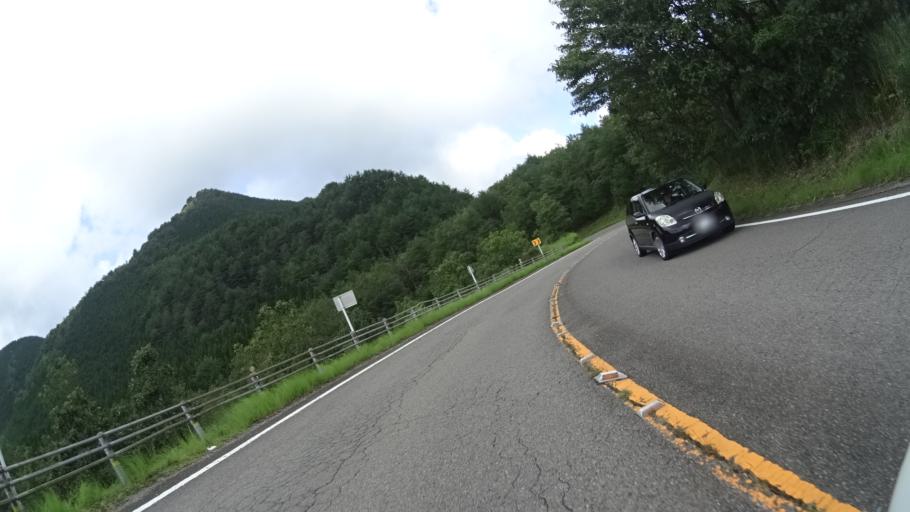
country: JP
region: Oita
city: Beppu
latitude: 33.2858
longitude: 131.3725
